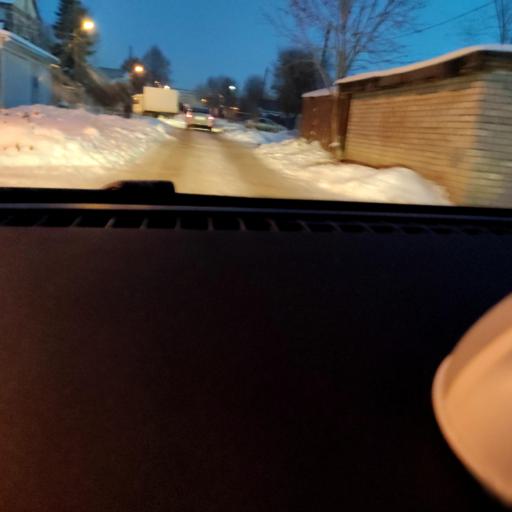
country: RU
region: Samara
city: Samara
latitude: 53.2027
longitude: 50.1962
